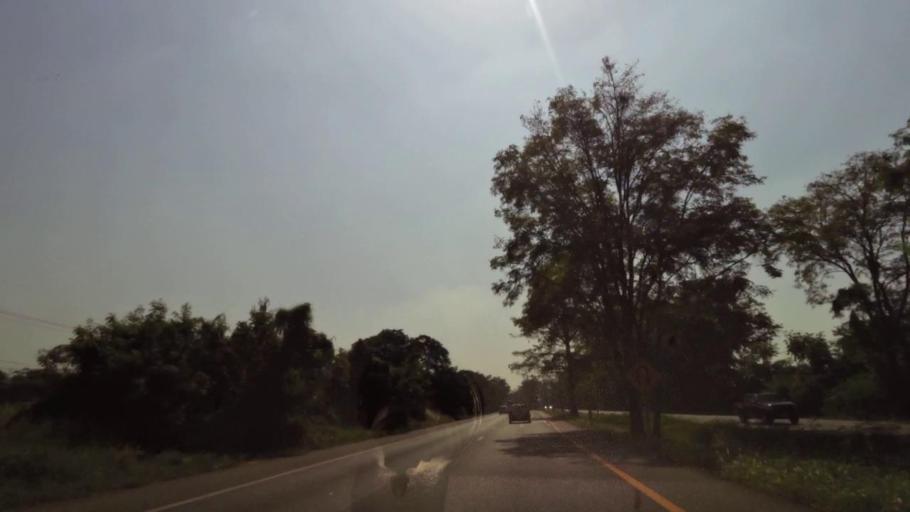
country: TH
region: Phichit
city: Bueng Na Rang
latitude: 16.0367
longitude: 100.1168
